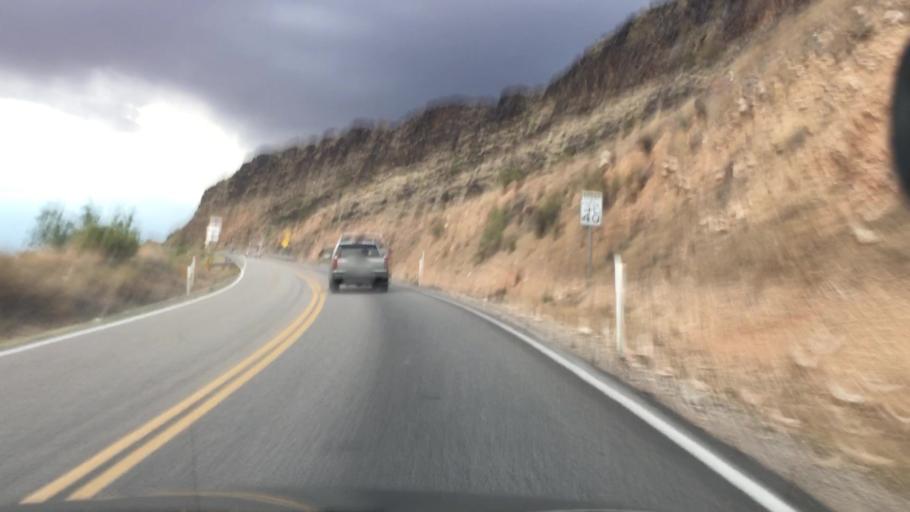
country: US
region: Utah
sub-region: Washington County
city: Hurricane
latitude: 37.1758
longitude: -113.2838
